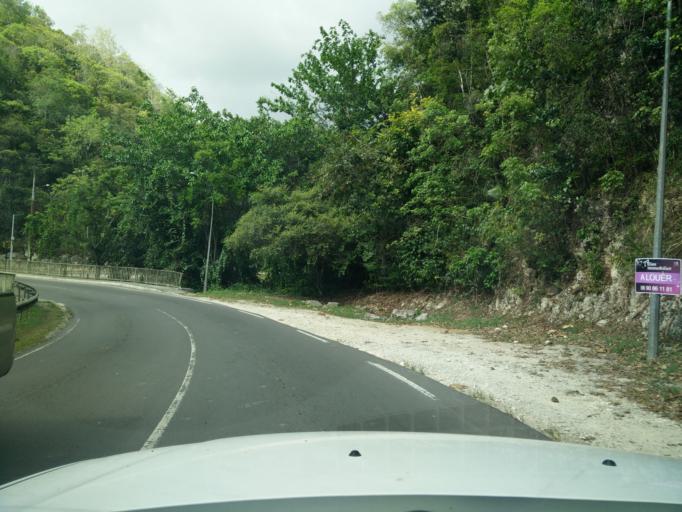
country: GP
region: Guadeloupe
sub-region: Guadeloupe
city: Le Gosier
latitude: 16.2176
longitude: -61.4777
